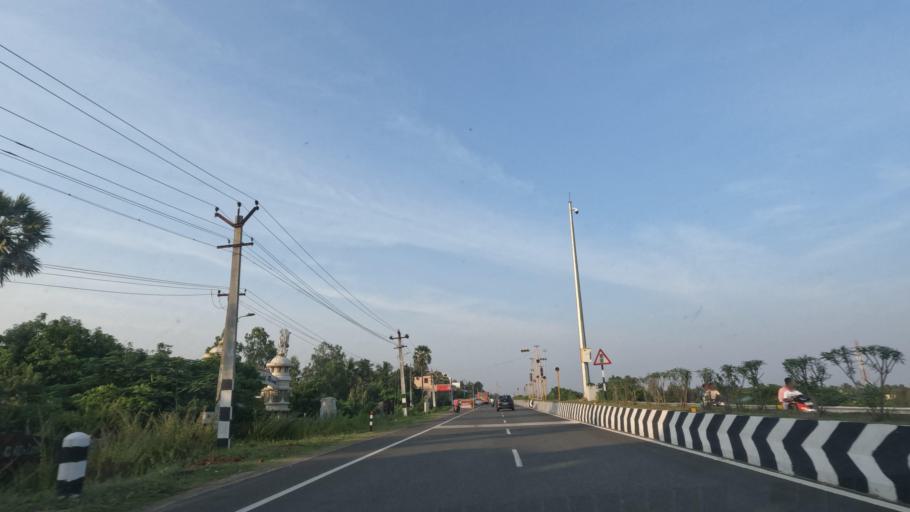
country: IN
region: Tamil Nadu
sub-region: Kancheepuram
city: Mamallapuram
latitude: 12.7163
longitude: 80.2272
